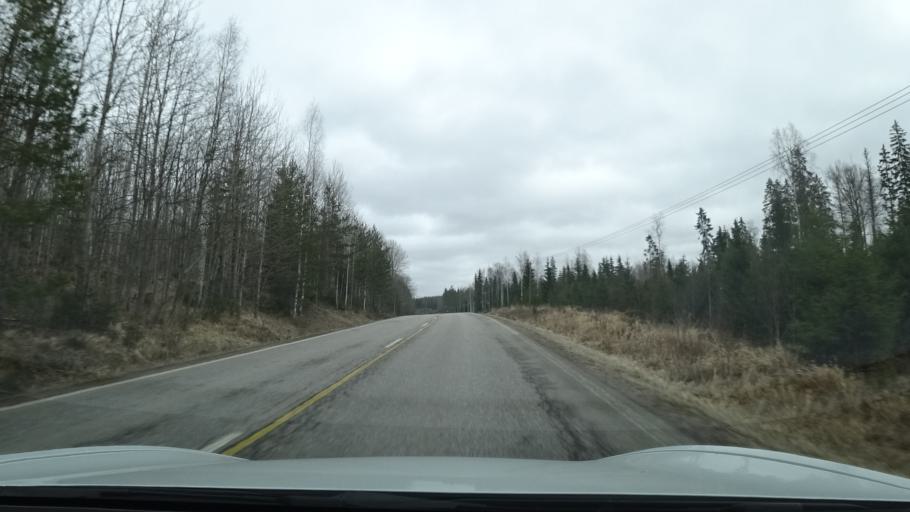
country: FI
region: Uusimaa
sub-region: Porvoo
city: Myrskylae
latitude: 60.6626
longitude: 25.7608
